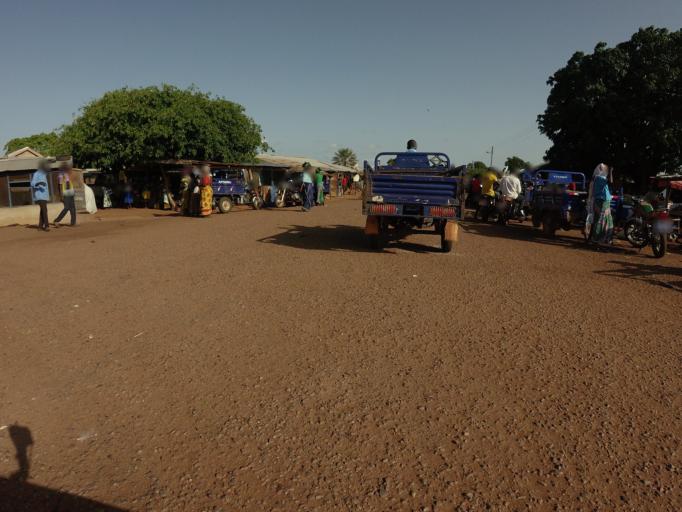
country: GH
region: Upper East
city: Bawku
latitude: 10.6326
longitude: -0.1805
